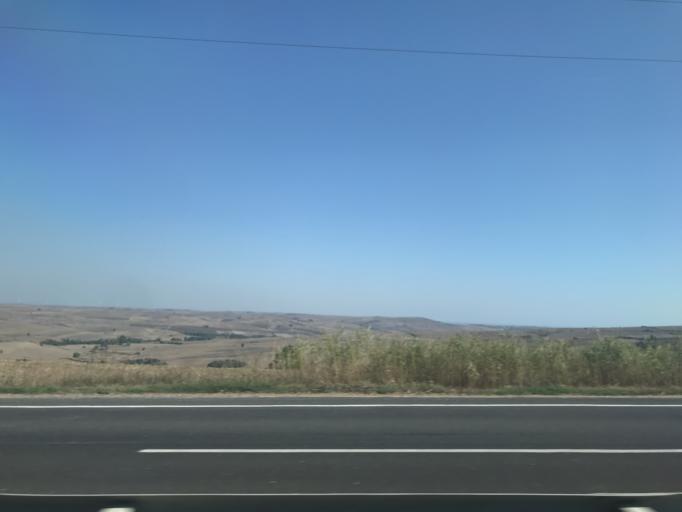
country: TR
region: Tekirdag
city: Tekirdag
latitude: 41.0469
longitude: 27.5075
